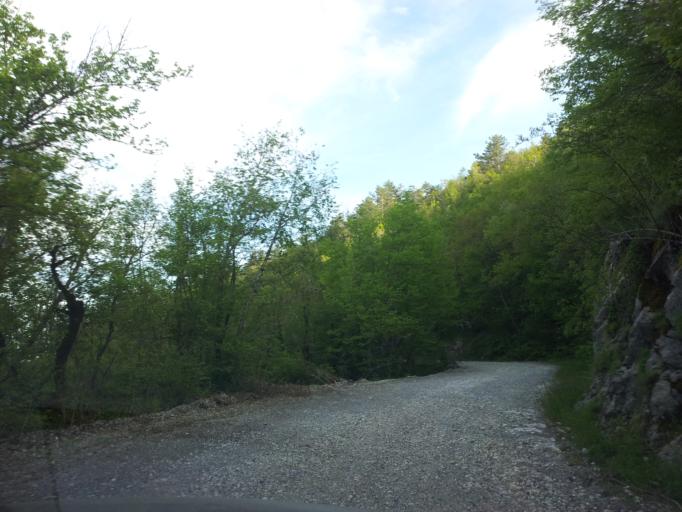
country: HR
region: Zadarska
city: Obrovac
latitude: 44.2997
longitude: 15.6642
